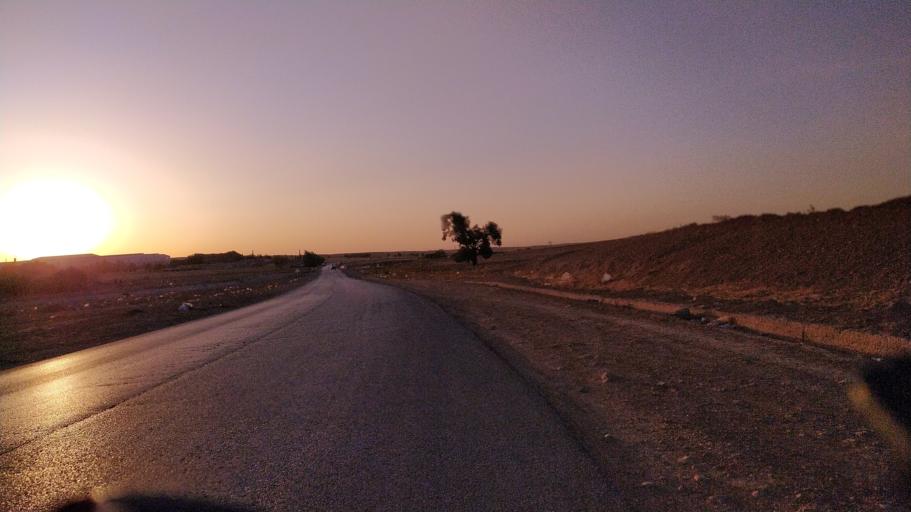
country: DZ
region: Tiaret
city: Frenda
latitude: 34.9016
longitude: 1.2424
